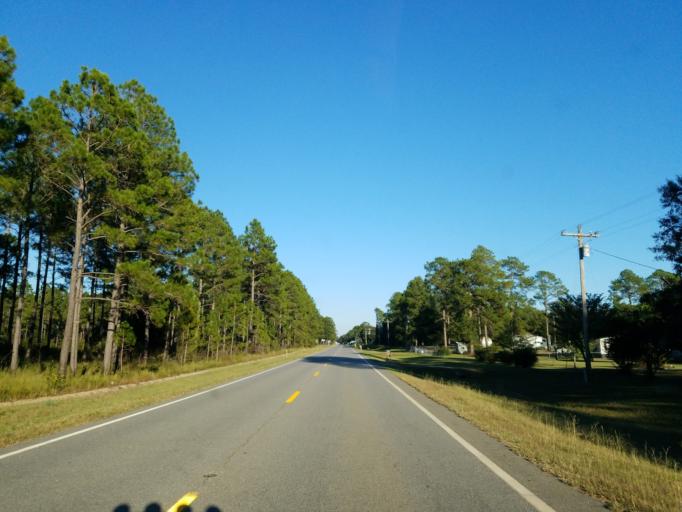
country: US
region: Georgia
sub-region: Lee County
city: Leesburg
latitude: 31.7269
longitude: -84.0513
